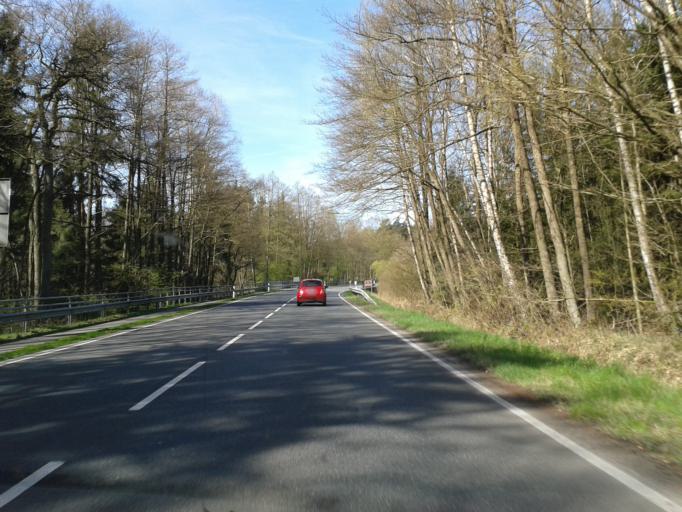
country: DE
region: Lower Saxony
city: Munster
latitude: 52.9550
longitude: 10.1232
